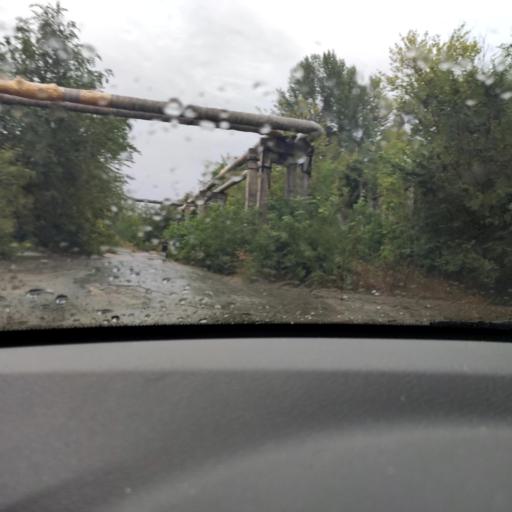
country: RU
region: Samara
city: Samara
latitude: 53.2213
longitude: 50.1483
